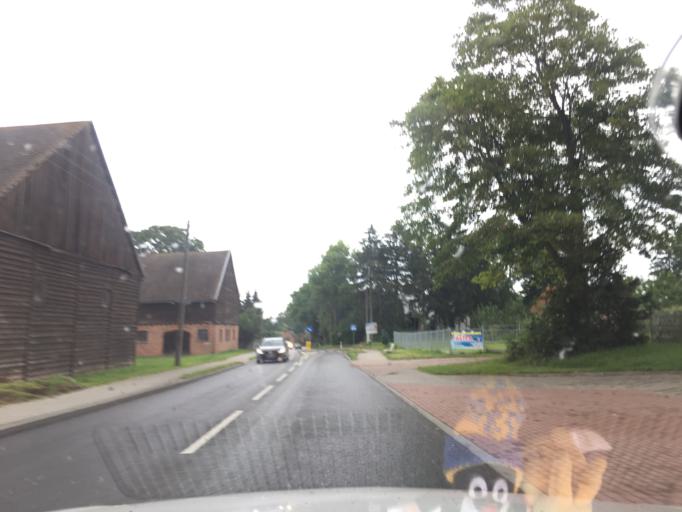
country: PL
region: West Pomeranian Voivodeship
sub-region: Powiat gryficki
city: Karnice
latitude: 54.0703
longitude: 15.0752
